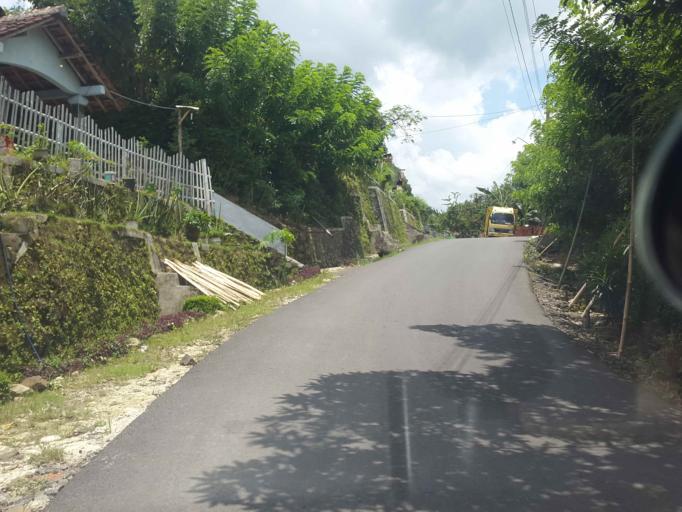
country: ID
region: Central Java
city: Karanggintung
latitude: -7.4407
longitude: 108.9420
